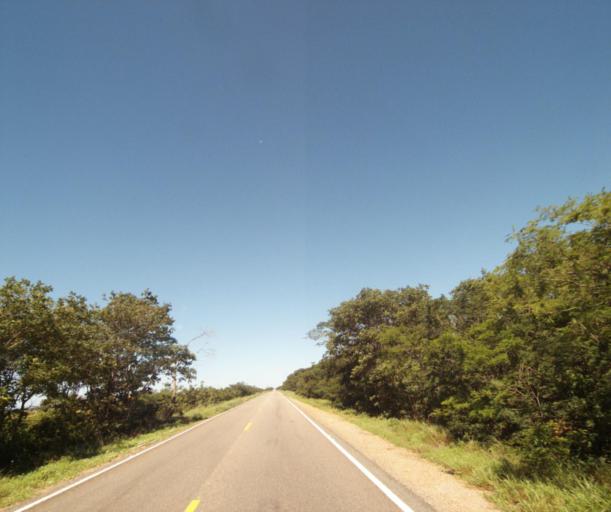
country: BR
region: Bahia
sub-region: Palmas De Monte Alto
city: Palmas de Monte Alto
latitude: -14.2650
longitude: -43.3517
